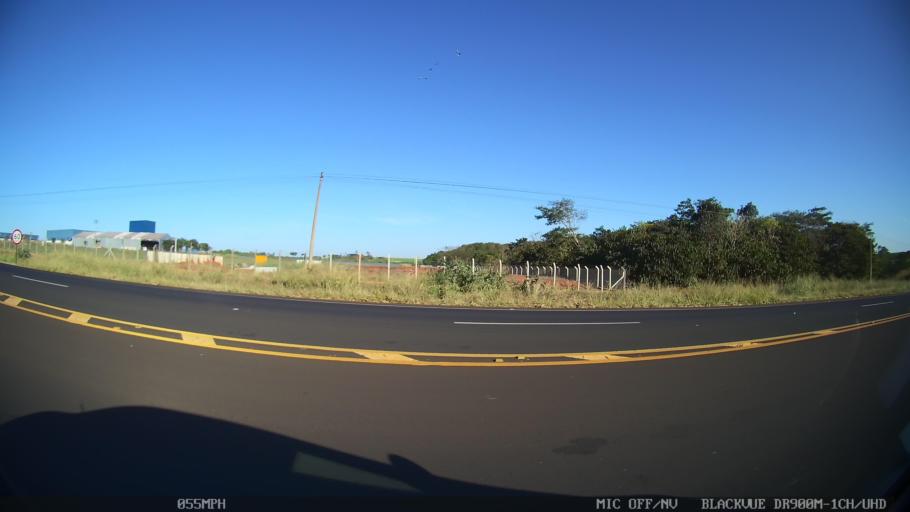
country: BR
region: Sao Paulo
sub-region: Olimpia
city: Olimpia
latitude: -20.7175
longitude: -49.0022
